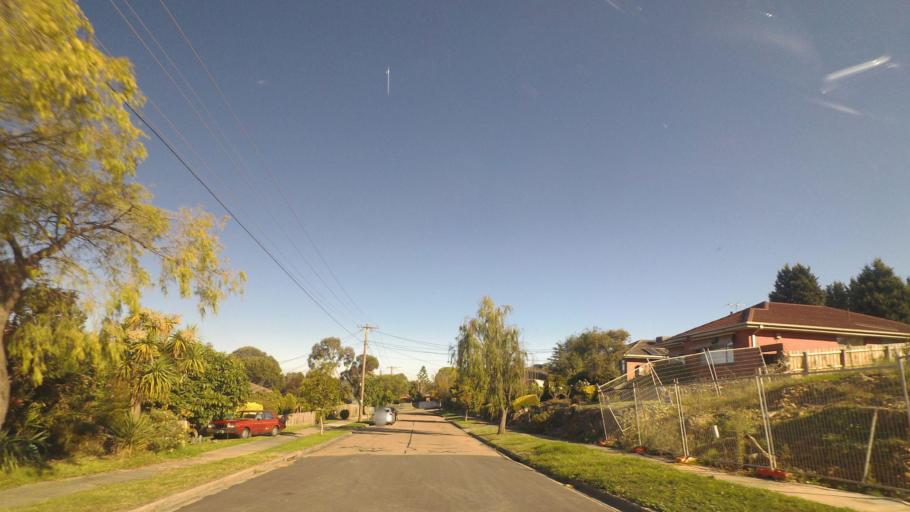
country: AU
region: Victoria
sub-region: Manningham
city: Doncaster East
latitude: -37.7943
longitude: 145.1529
